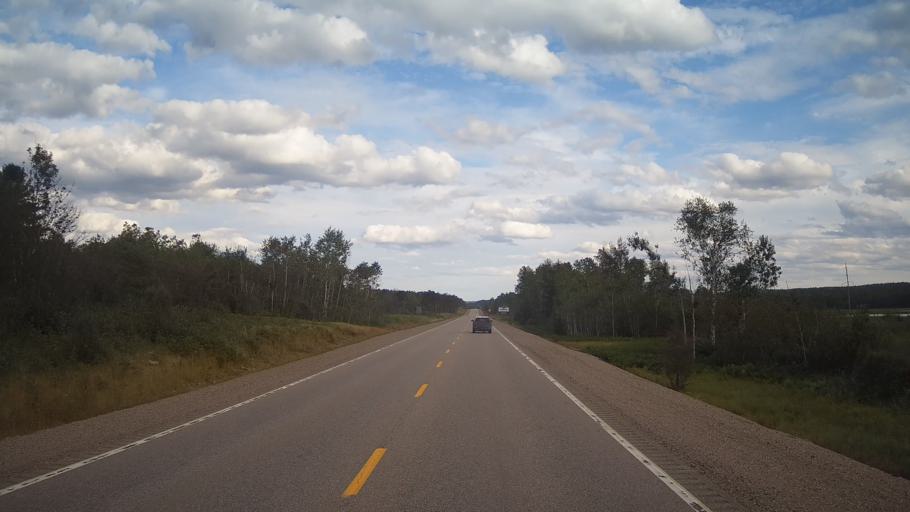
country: CA
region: Ontario
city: Mattawa
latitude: 46.2763
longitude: -78.3736
